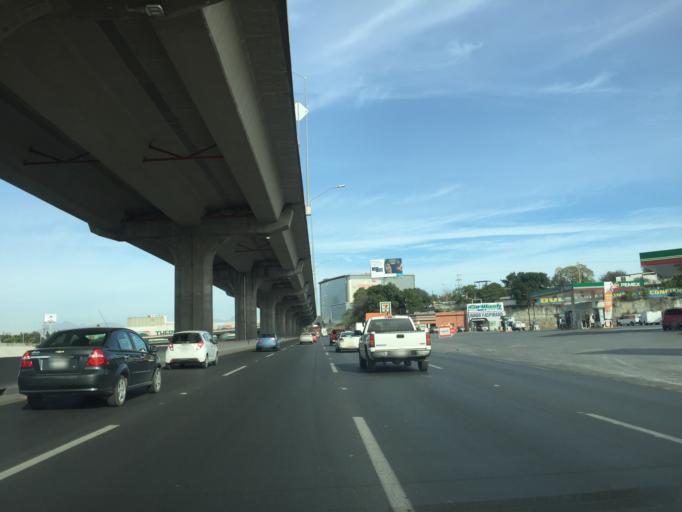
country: MX
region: Nuevo Leon
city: Guadalupe
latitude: 25.6909
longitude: -100.2214
